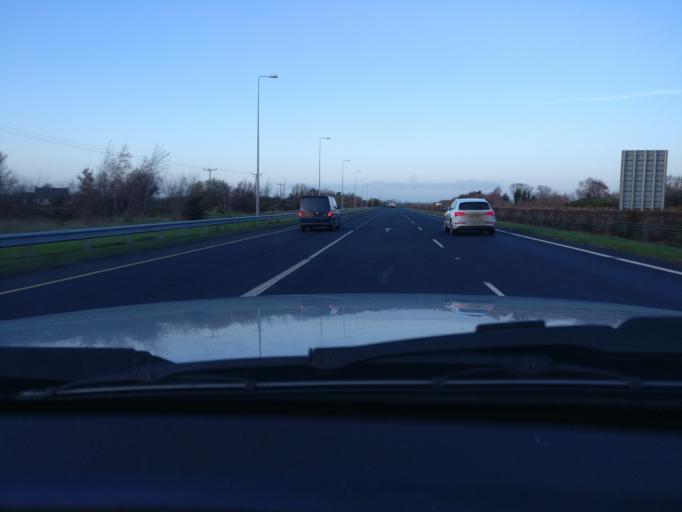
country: IE
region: Leinster
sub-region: Lu
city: Dromiskin
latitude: 53.9344
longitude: -6.4150
